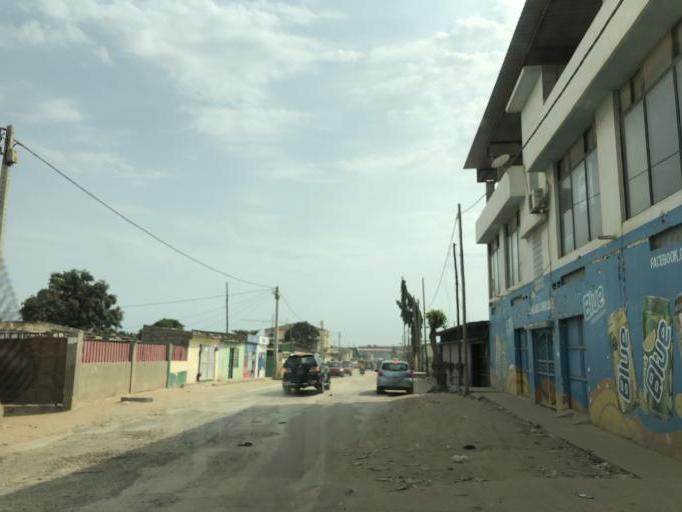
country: AO
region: Luanda
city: Luanda
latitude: -8.8991
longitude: 13.3497
